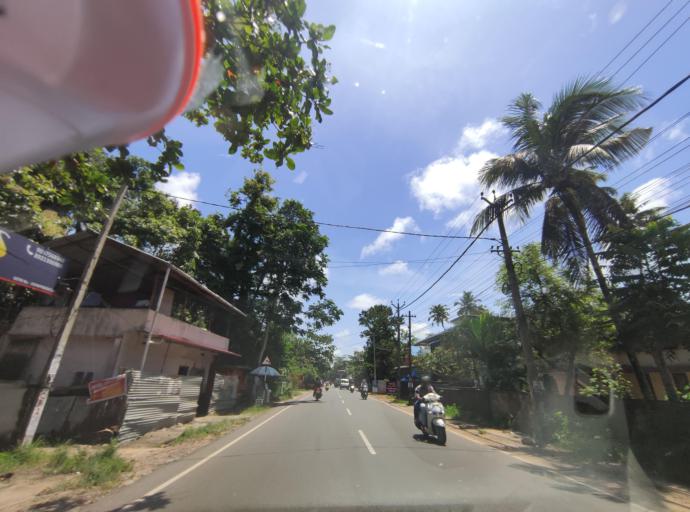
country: IN
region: Kerala
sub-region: Alappuzha
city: Alleppey
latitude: 9.5223
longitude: 76.3400
